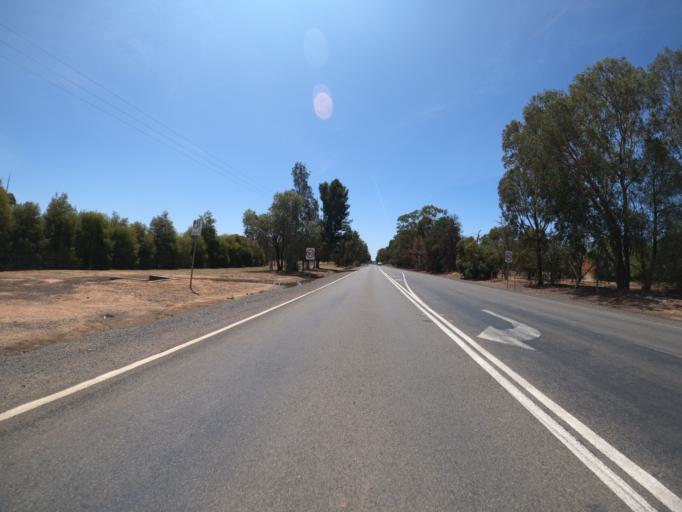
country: AU
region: Victoria
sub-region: Moira
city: Yarrawonga
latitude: -36.0404
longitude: 145.9954
